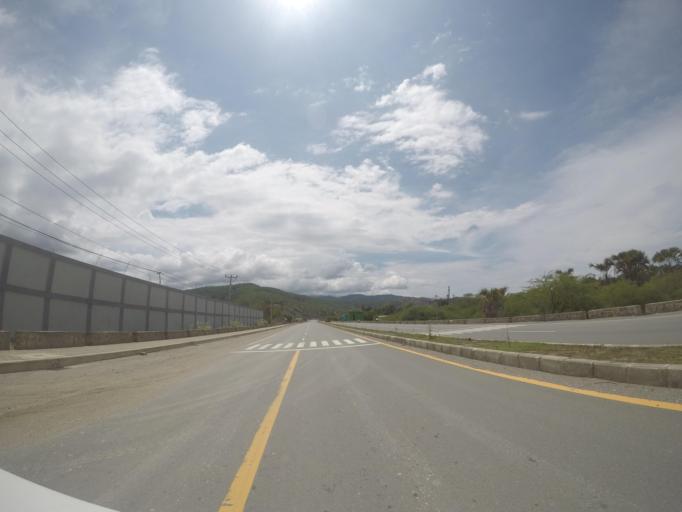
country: TL
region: Dili
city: Dili
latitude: -8.5697
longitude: 125.4886
